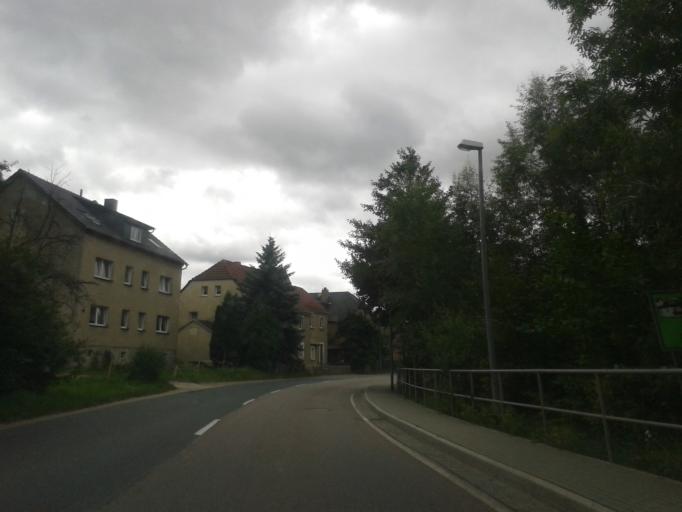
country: DE
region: Saxony
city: Wilsdruff
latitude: 51.0198
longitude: 13.5587
